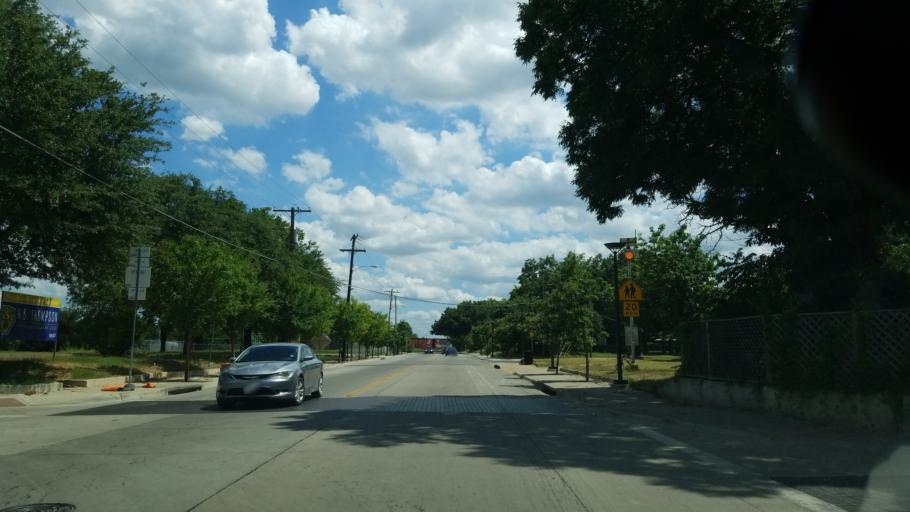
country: US
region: Texas
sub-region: Dallas County
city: Dallas
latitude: 32.7468
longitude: -96.7535
